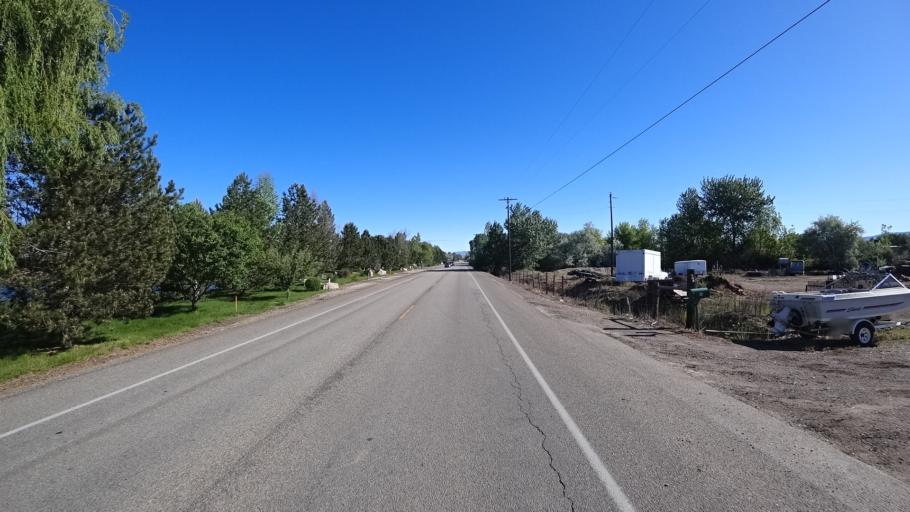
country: US
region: Idaho
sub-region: Ada County
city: Eagle
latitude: 43.6774
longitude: -116.4137
